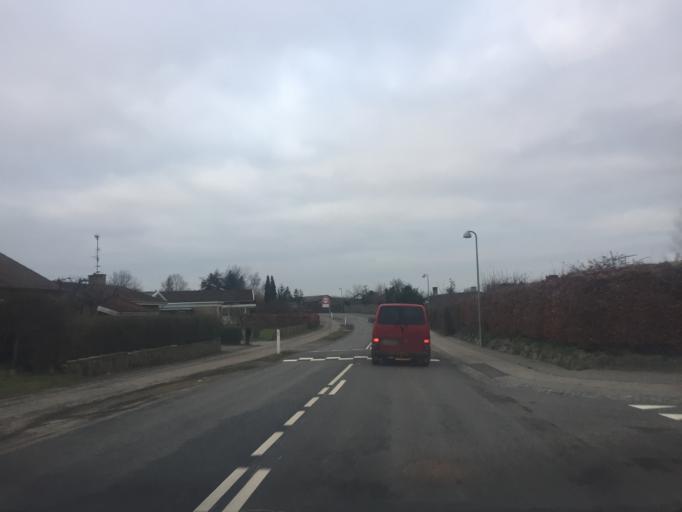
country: DK
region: Zealand
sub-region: Roskilde Kommune
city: Gundsomagle
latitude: 55.7392
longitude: 12.1518
